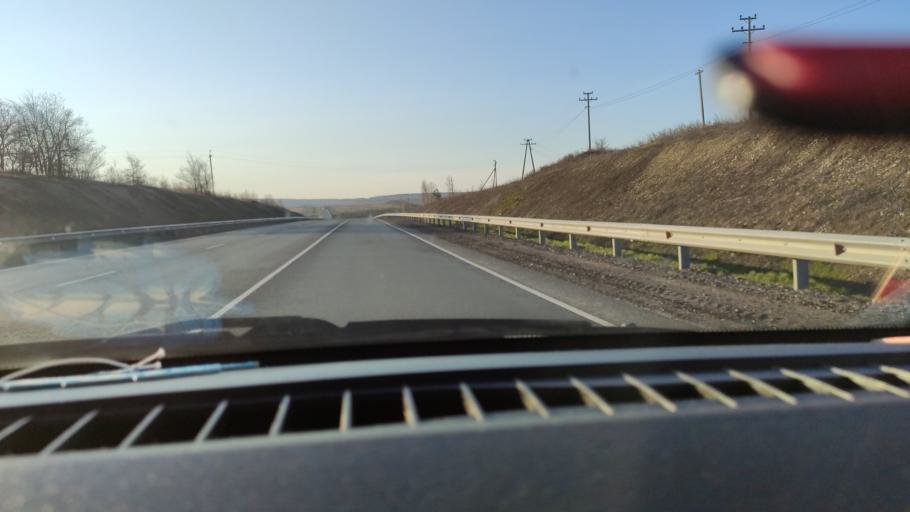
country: RU
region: Saratov
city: Shikhany
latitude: 52.1435
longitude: 47.2022
